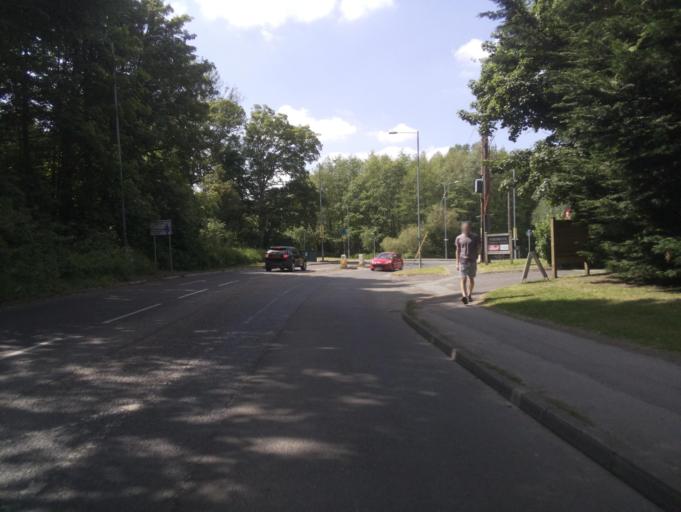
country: GB
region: England
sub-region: Wiltshire
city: Pewsey
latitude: 51.3432
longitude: -1.7716
